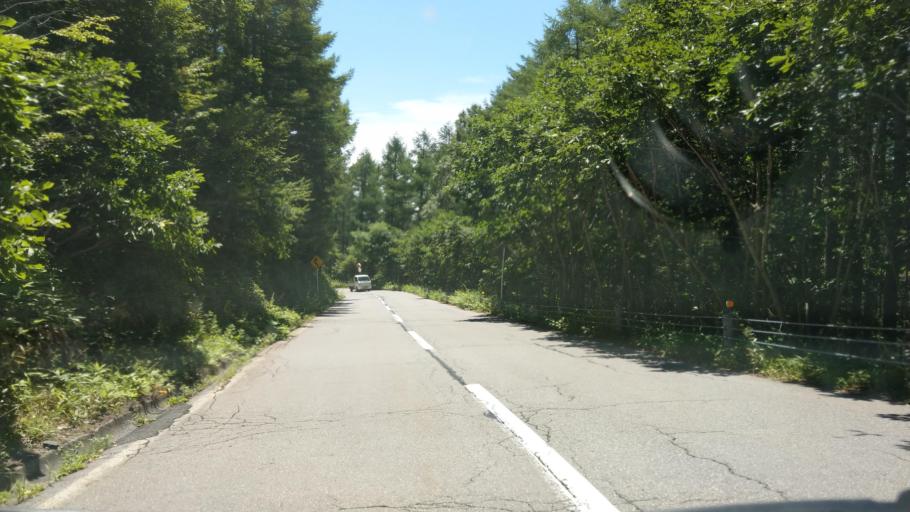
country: JP
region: Nagano
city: Komoro
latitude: 36.3954
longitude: 138.4665
